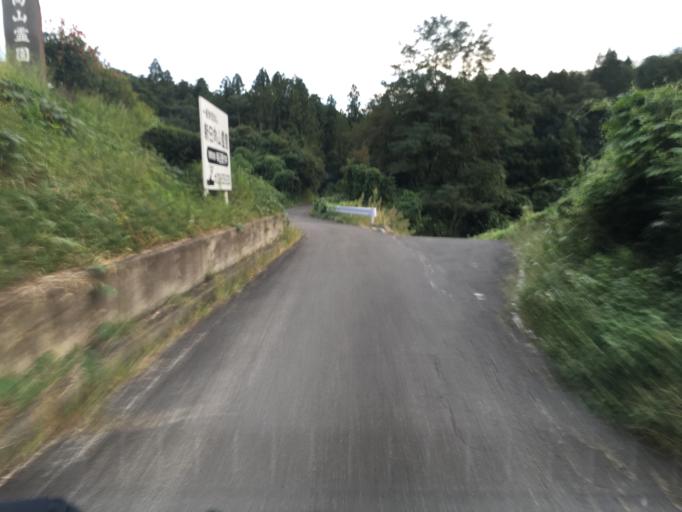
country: JP
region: Fukushima
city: Fukushima-shi
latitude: 37.7632
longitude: 140.5006
